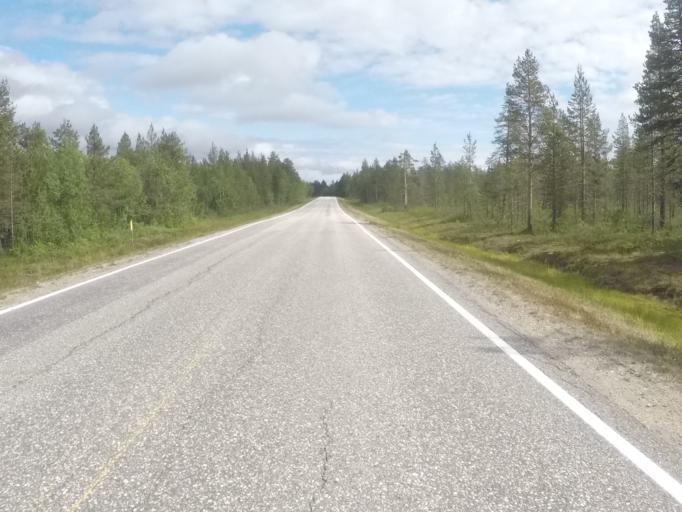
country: FI
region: Lapland
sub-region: Tunturi-Lappi
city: Enontekioe
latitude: 68.3020
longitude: 23.1550
